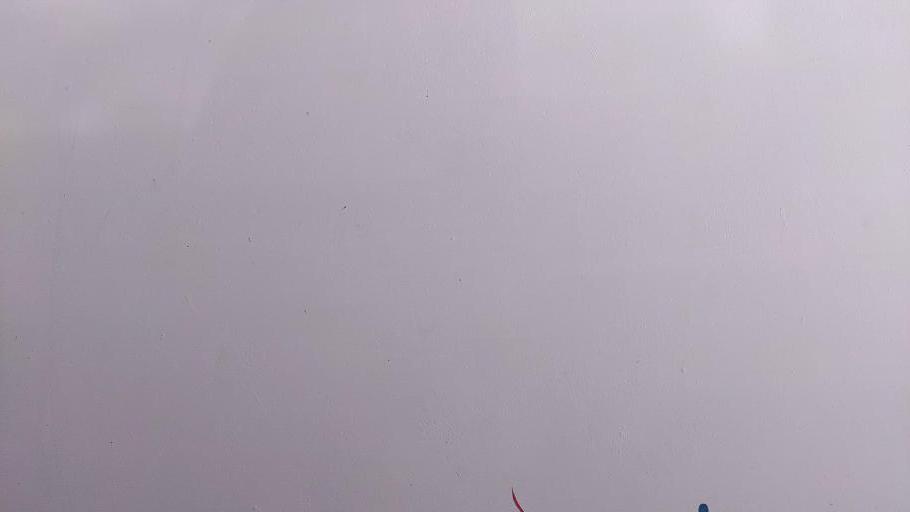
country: IN
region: Kerala
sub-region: Thrissur District
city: Trichur
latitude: 10.5037
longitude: 76.1461
